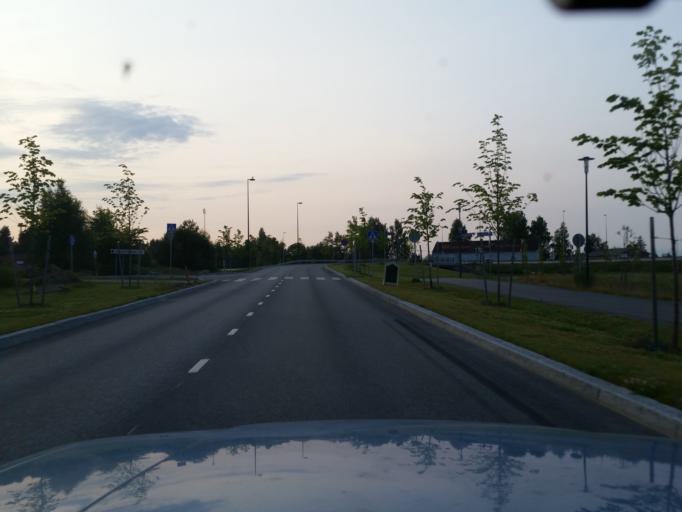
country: FI
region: Southern Savonia
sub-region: Savonlinna
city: Savonlinna
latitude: 61.8749
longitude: 28.8746
